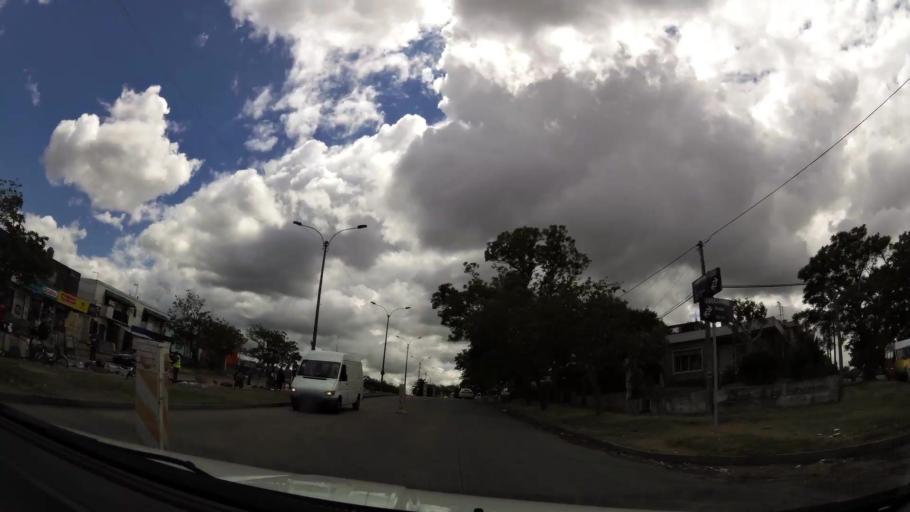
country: UY
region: Montevideo
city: Montevideo
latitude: -34.8310
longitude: -56.1427
